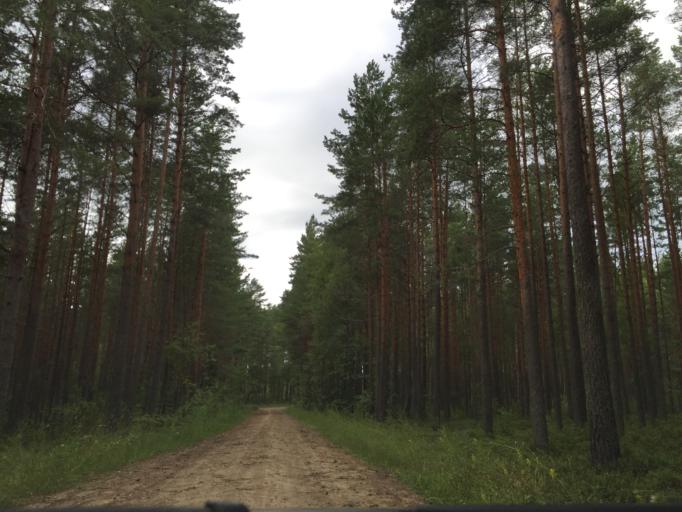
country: LV
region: Saulkrastu
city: Saulkrasti
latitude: 57.2188
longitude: 24.4141
